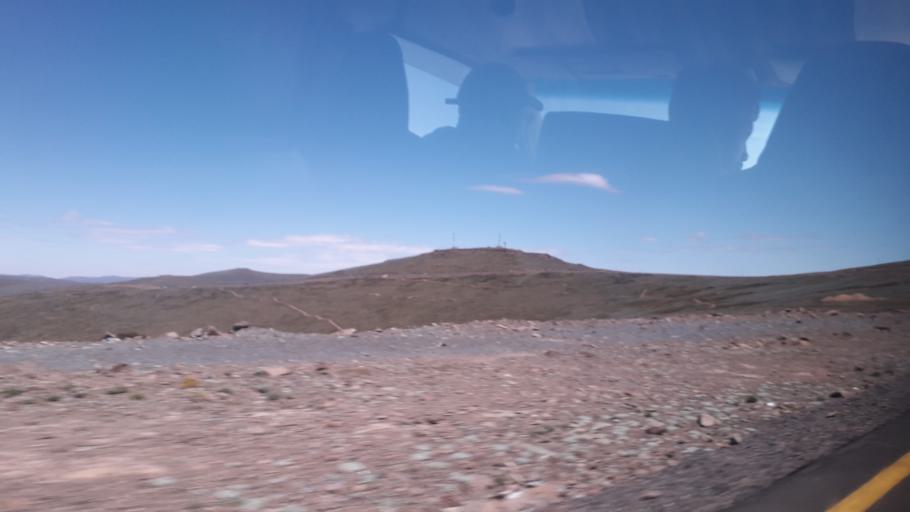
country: ZA
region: Orange Free State
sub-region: Thabo Mofutsanyana District Municipality
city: Phuthaditjhaba
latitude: -28.8123
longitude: 28.7345
